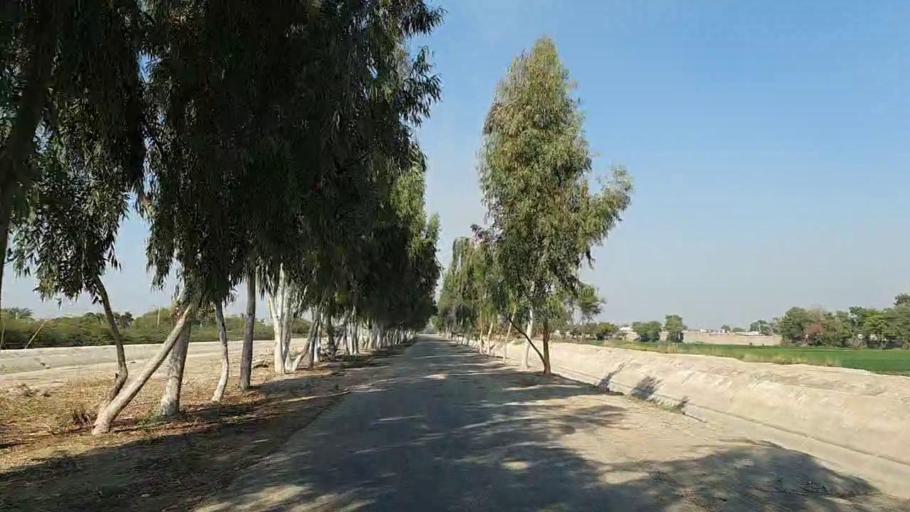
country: PK
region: Sindh
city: Nawabshah
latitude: 26.3453
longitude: 68.3809
